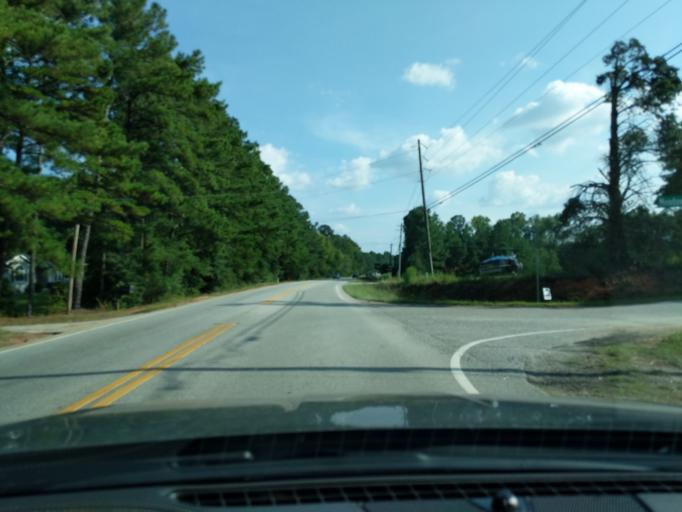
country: US
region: Georgia
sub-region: Columbia County
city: Grovetown
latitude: 33.5033
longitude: -82.2002
